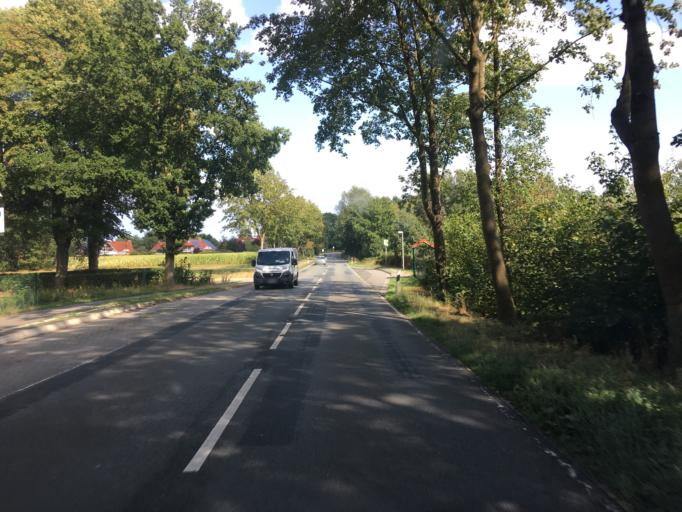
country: DE
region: Lower Saxony
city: Wardenburg
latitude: 53.0674
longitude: 8.1819
